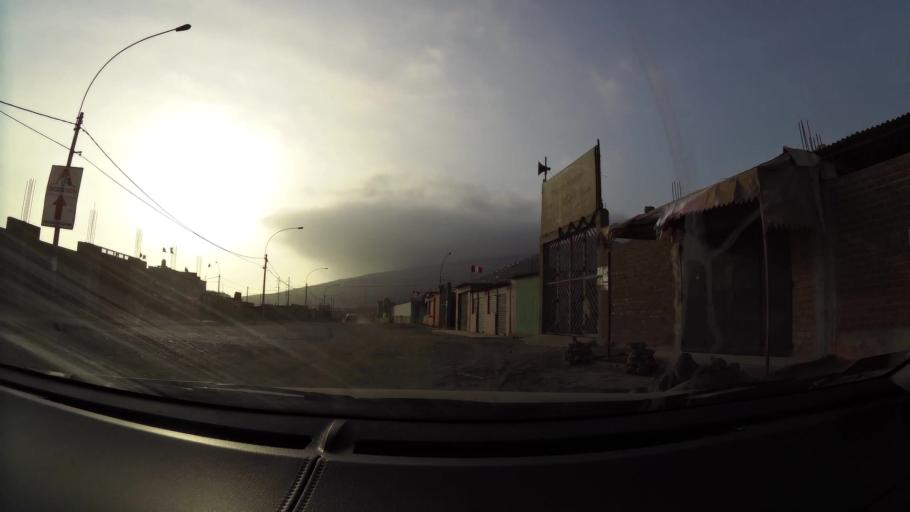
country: PE
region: Lima
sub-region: Lima
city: Santa Rosa
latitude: -11.7462
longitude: -77.1475
